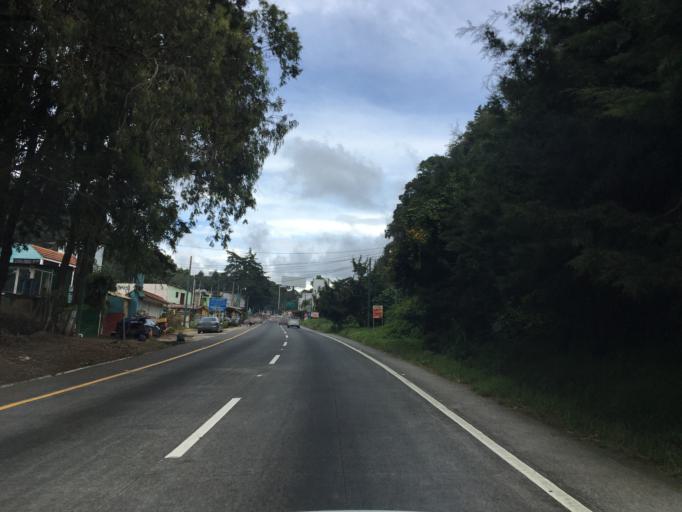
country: GT
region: Sacatepequez
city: Santa Lucia Milpas Altas
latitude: 14.5792
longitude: -90.6650
